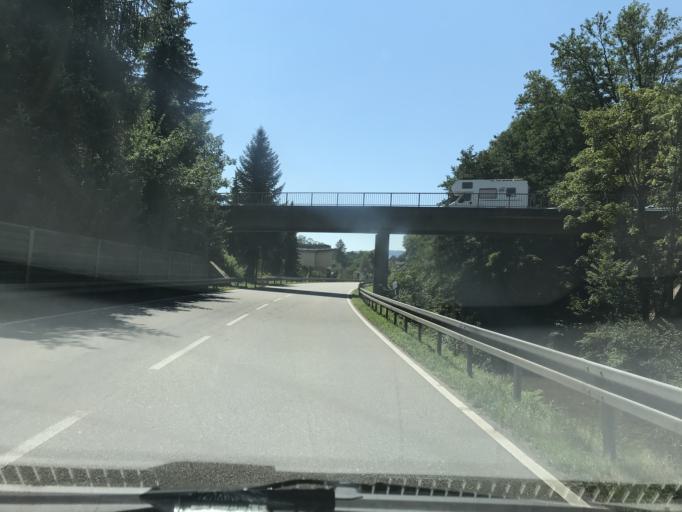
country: DE
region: Baden-Wuerttemberg
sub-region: Freiburg Region
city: Schworstadt
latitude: 47.5949
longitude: 7.9124
